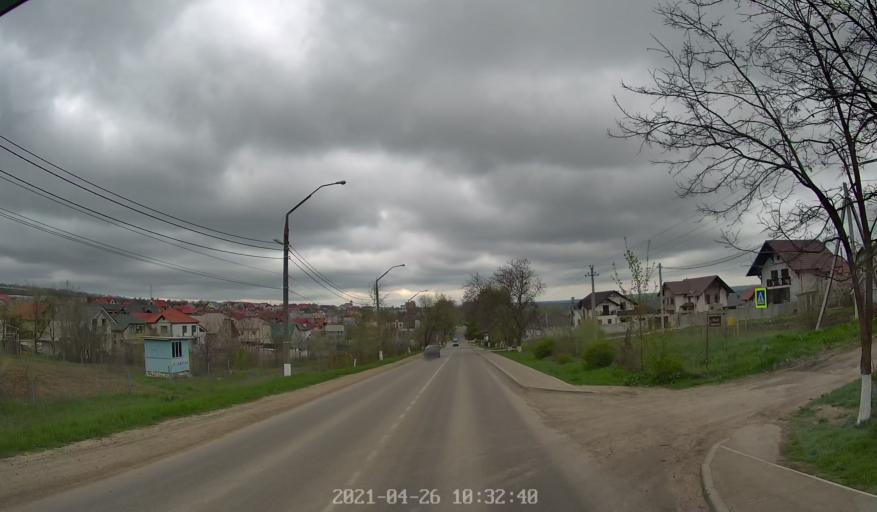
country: MD
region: Chisinau
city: Cricova
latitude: 47.1222
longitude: 28.8664
